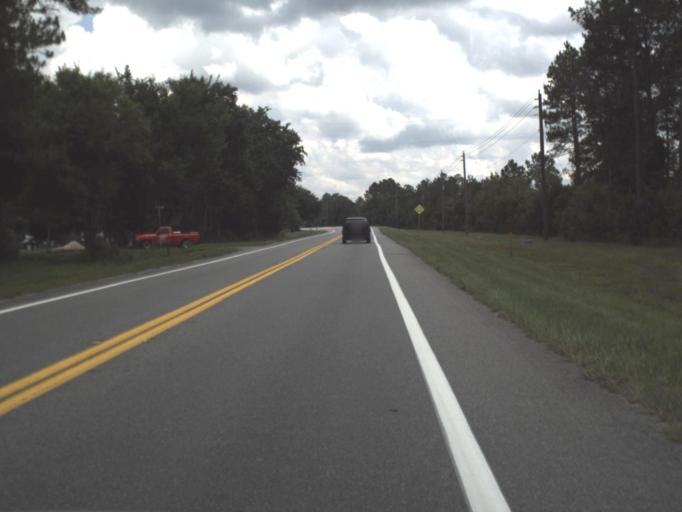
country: US
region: Florida
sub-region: Union County
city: Lake Butler
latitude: 30.0463
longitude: -82.2959
